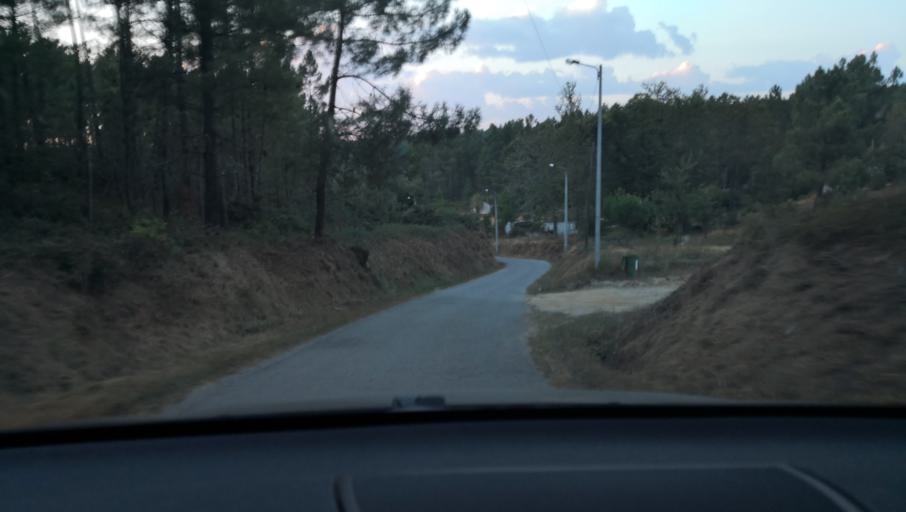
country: PT
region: Vila Real
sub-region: Sabrosa
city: Vilela
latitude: 41.2468
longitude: -7.6303
